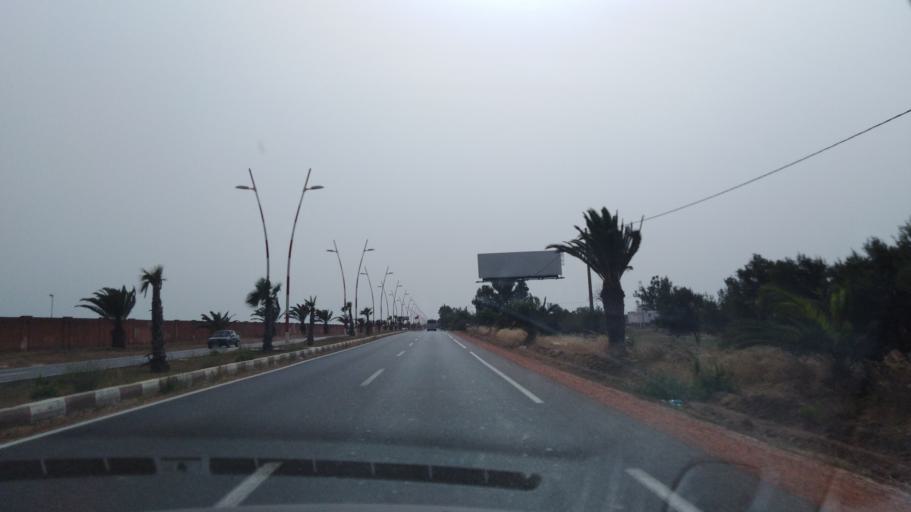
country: MA
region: Chaouia-Ouardigha
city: Nouaseur
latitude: 33.3937
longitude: -7.5982
